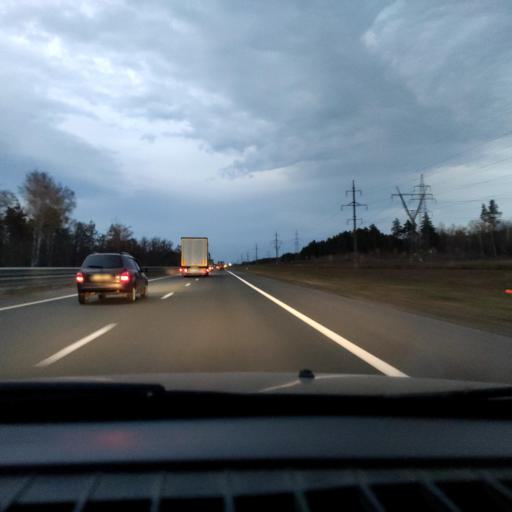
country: RU
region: Samara
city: Povolzhskiy
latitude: 53.5161
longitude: 49.7038
